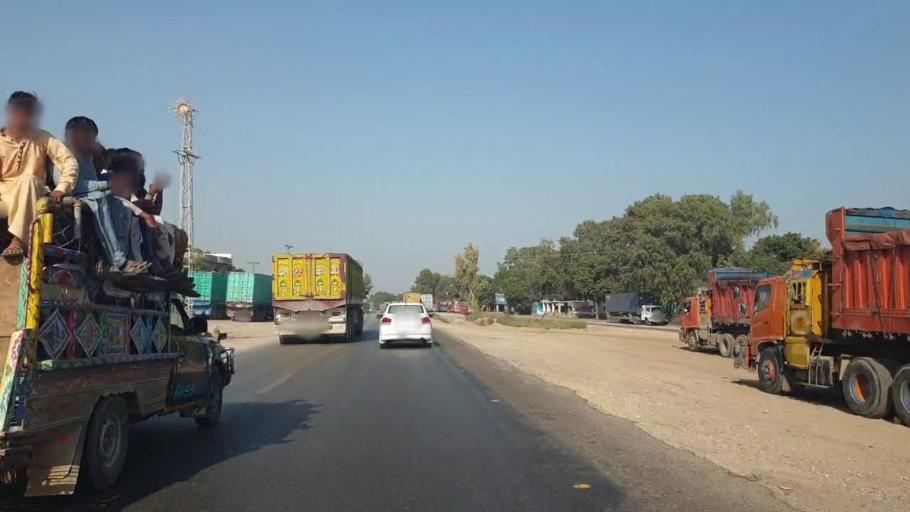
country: PK
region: Sindh
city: Matiari
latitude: 25.5123
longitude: 68.4286
